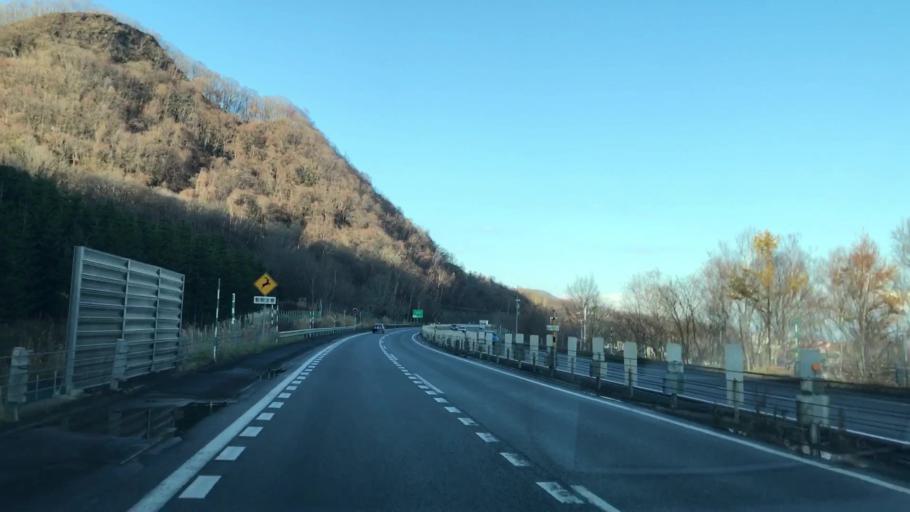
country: JP
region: Hokkaido
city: Sapporo
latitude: 43.1285
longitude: 141.1910
